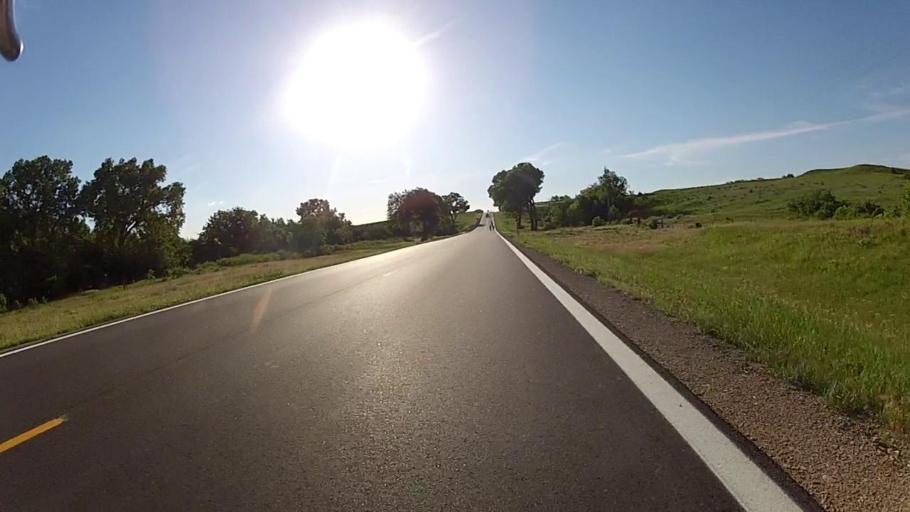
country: US
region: Kansas
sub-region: Comanche County
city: Coldwater
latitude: 37.2819
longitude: -99.0771
